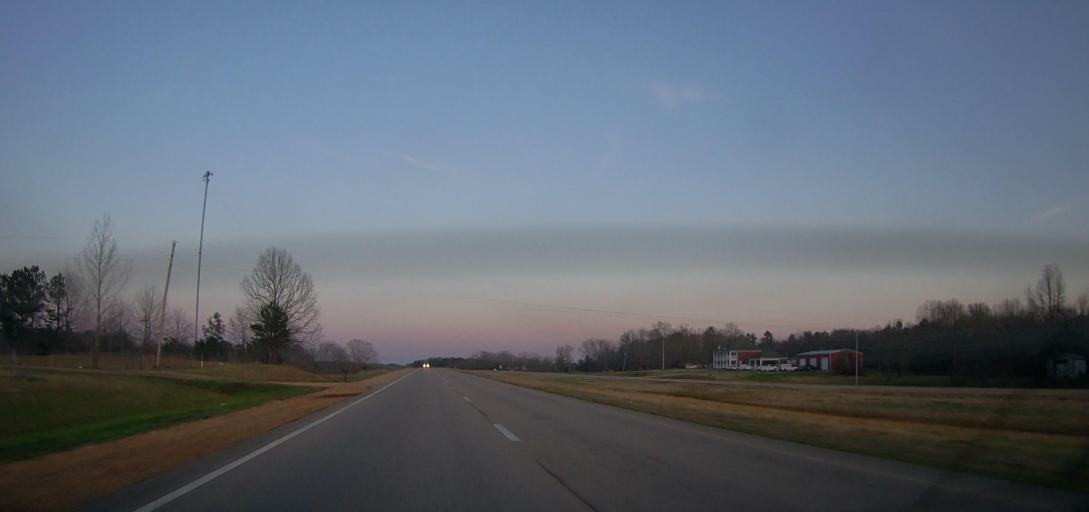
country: US
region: Mississippi
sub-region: Tippah County
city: Ripley
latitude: 34.9480
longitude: -88.8066
